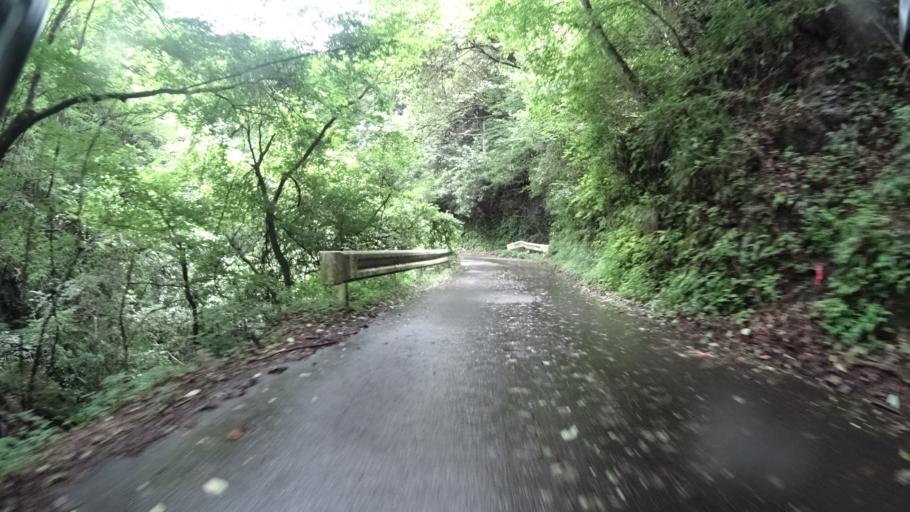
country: JP
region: Saitama
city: Chichibu
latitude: 35.8806
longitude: 139.1439
